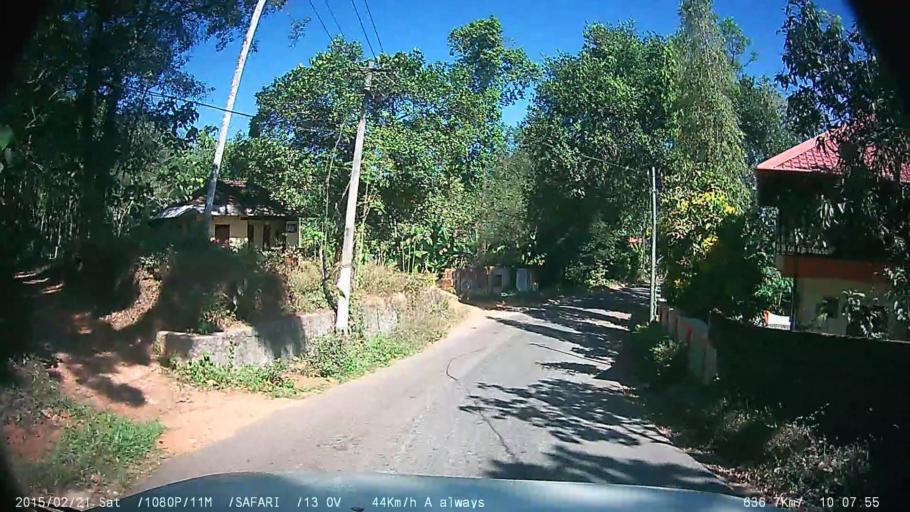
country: IN
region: Kerala
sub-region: Ernakulam
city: Piravam
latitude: 9.8756
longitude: 76.6064
